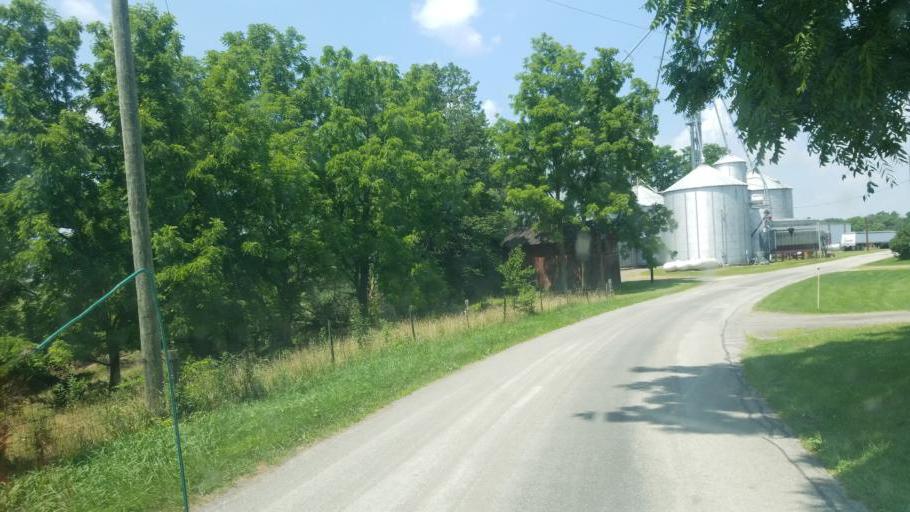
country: US
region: Ohio
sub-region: Richland County
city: Shelby
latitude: 40.8469
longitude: -82.6578
